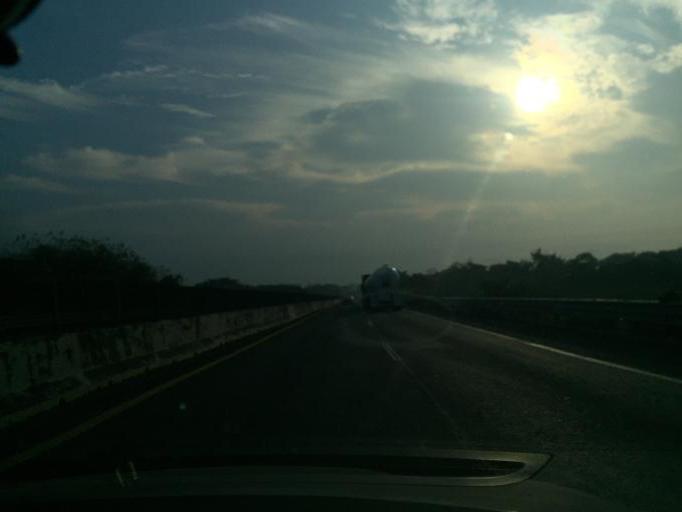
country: MX
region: Veracruz
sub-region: Tierra Blanca
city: Huixcolotla
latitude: 18.7849
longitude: -96.4971
